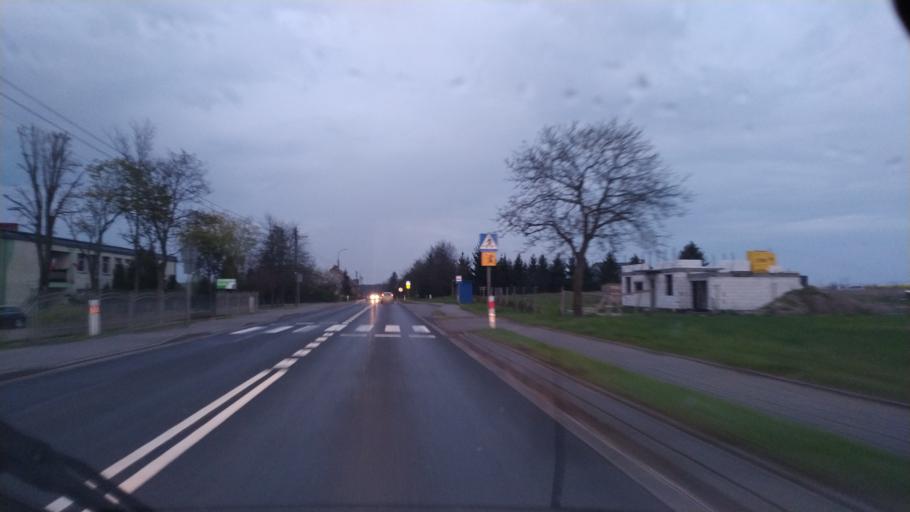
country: PL
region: Greater Poland Voivodeship
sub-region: Powiat pilski
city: Szydlowo
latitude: 53.2472
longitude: 16.5862
